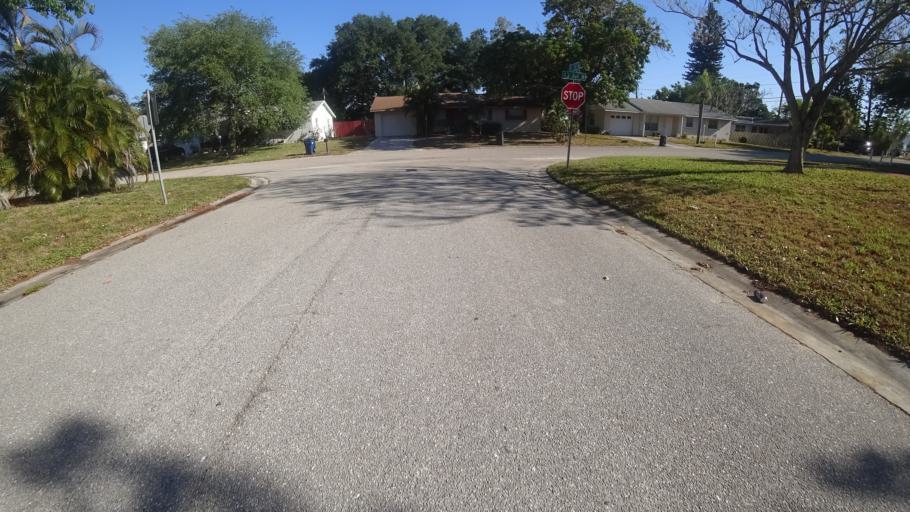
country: US
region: Florida
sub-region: Manatee County
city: Cortez
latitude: 27.4640
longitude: -82.6444
